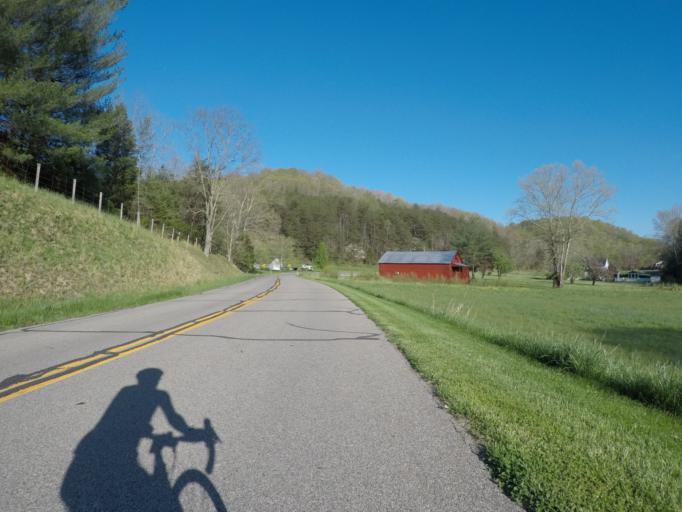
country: US
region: Kentucky
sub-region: Boyd County
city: Meads
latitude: 38.3661
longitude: -82.6799
